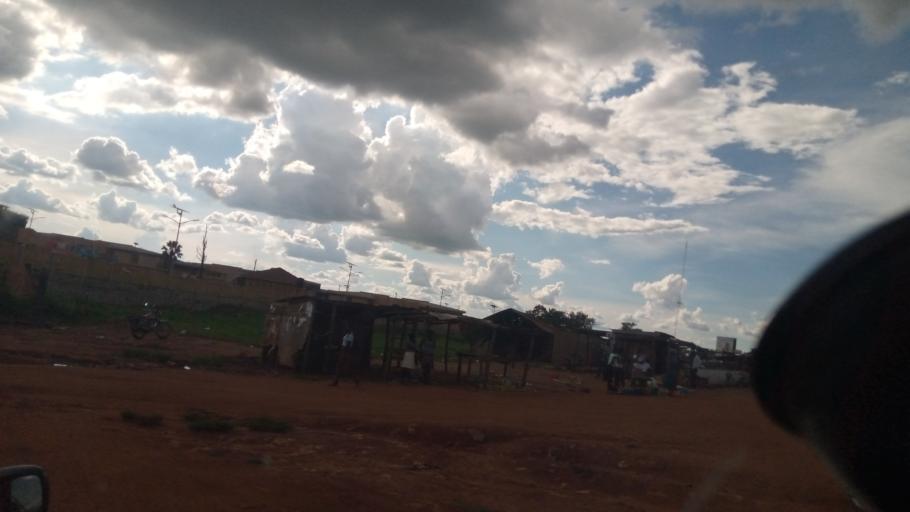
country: UG
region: Northern Region
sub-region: Lira District
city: Lira
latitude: 2.2426
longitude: 32.8999
